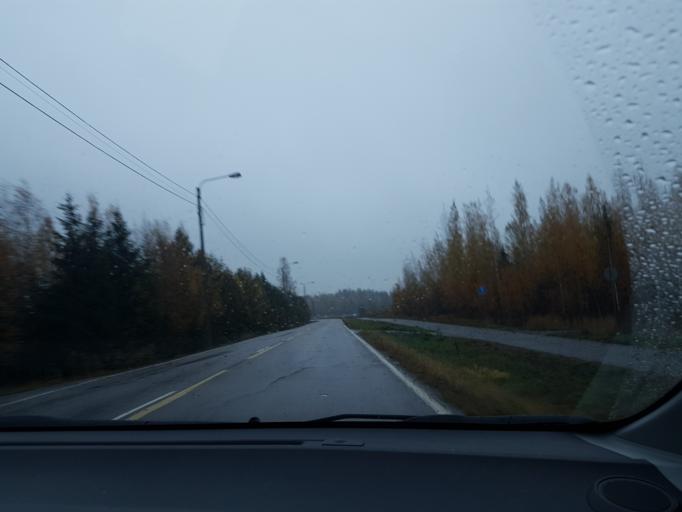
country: FI
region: Uusimaa
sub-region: Helsinki
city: Jaervenpaeae
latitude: 60.5514
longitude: 25.1256
